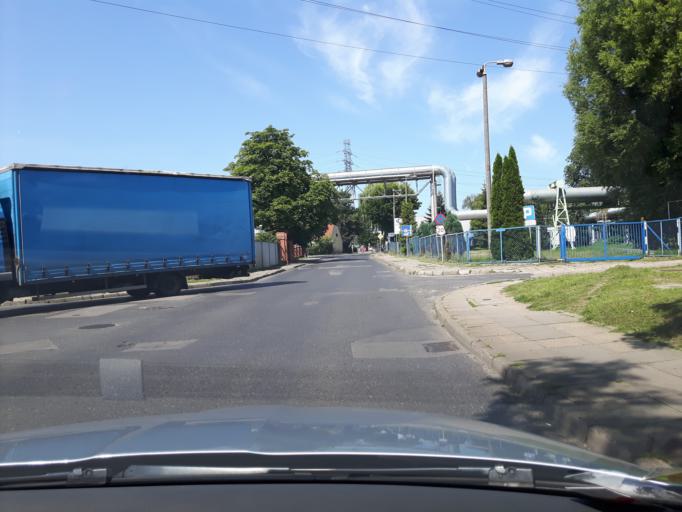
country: PL
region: Pomeranian Voivodeship
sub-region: Gdansk
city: Gdansk
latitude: 54.3779
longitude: 18.6367
